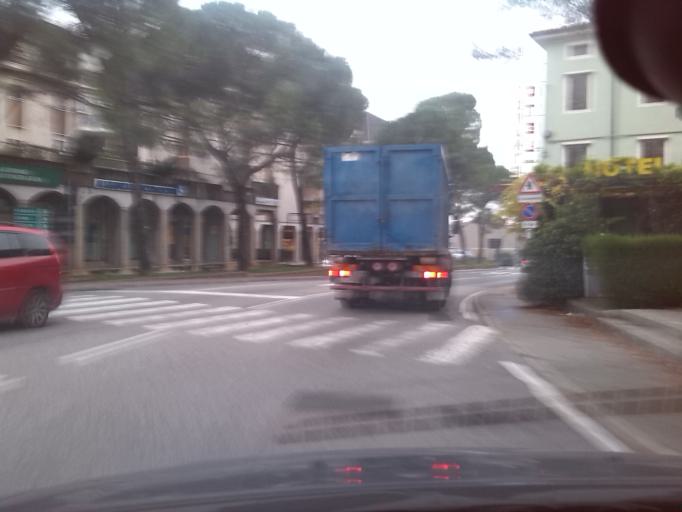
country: IT
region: Friuli Venezia Giulia
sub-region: Provincia di Gorizia
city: Gradisca d'Isonzo
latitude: 45.8882
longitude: 13.5011
